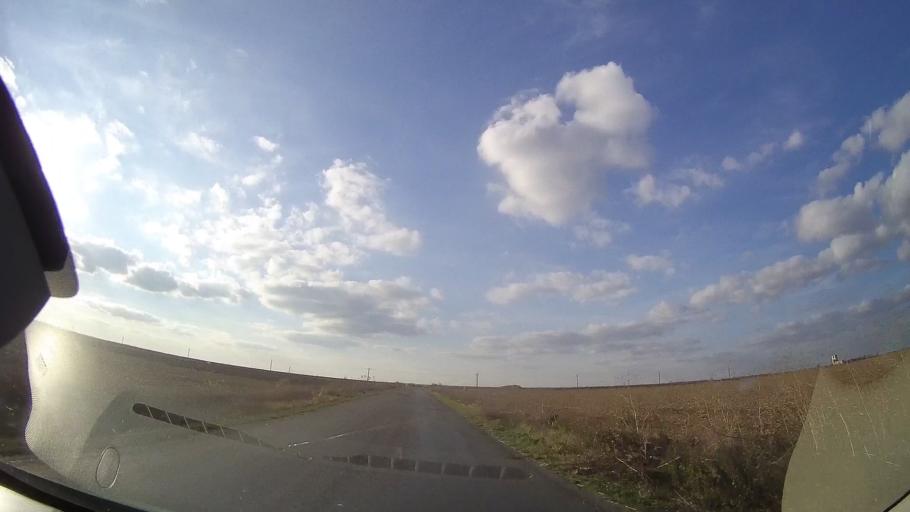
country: RO
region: Constanta
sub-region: Comuna Cerchezu
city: Cerchezu
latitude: 43.8259
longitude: 28.1277
